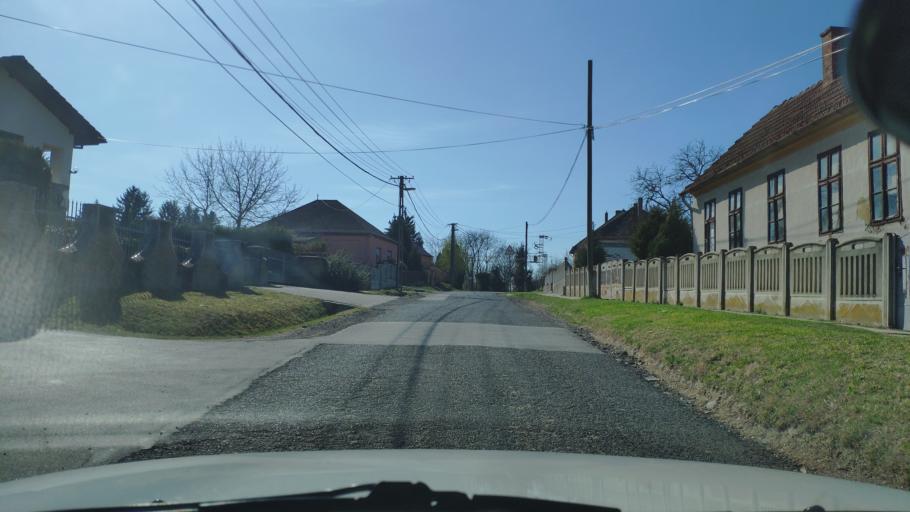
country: HU
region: Zala
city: Nagykanizsa
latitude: 46.4107
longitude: 16.9838
